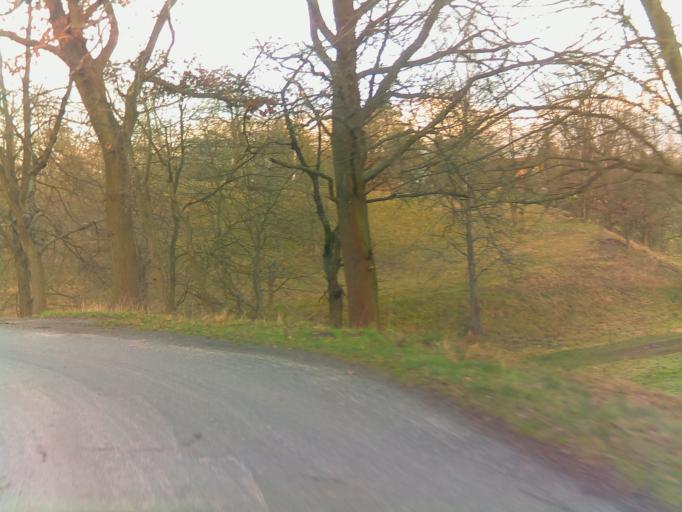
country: DE
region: Thuringia
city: Rudolstadt
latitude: 50.7592
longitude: 11.3496
